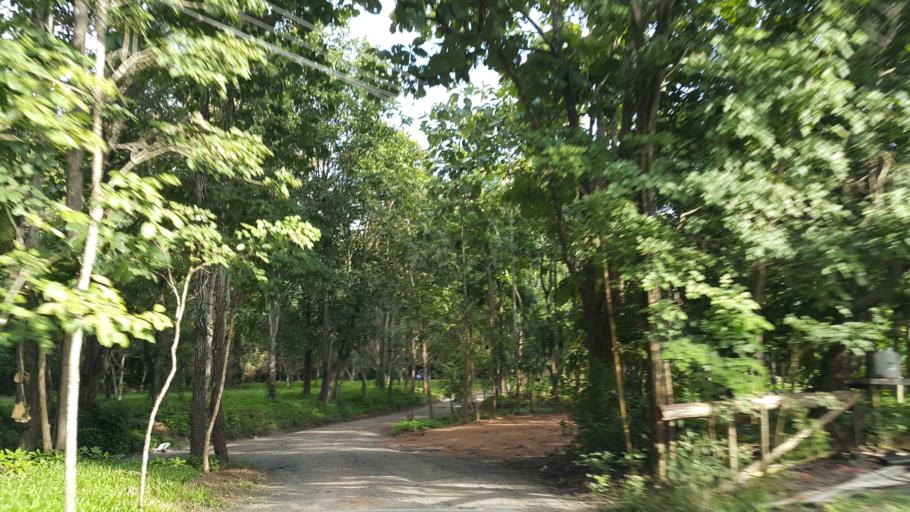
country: TH
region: Chiang Mai
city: Mae On
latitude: 18.8745
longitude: 99.2156
